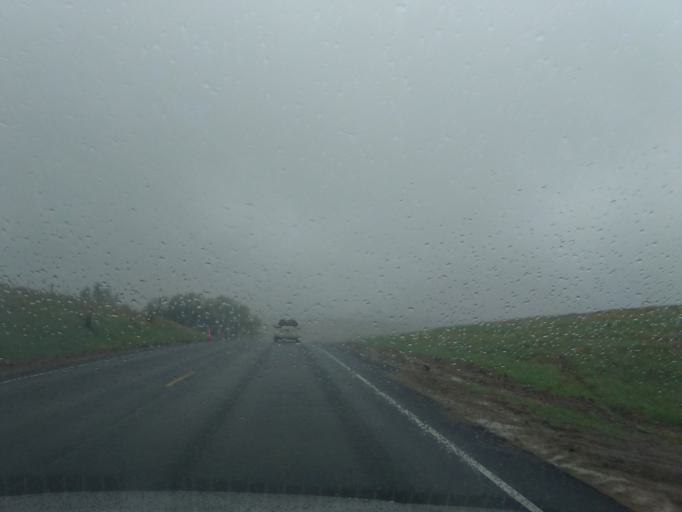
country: US
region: Nebraska
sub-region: Wayne County
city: Wayne
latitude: 42.1812
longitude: -97.1820
